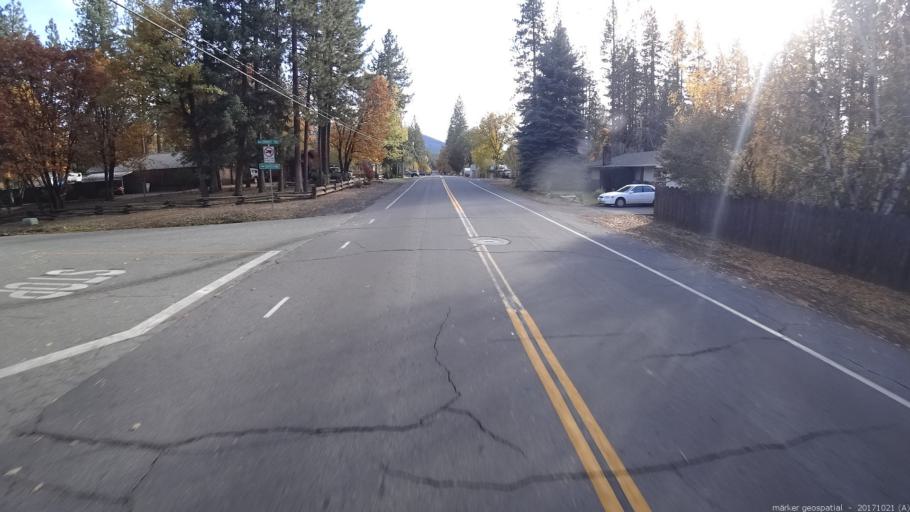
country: US
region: California
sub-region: Shasta County
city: Burney
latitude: 40.8811
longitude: -121.6575
